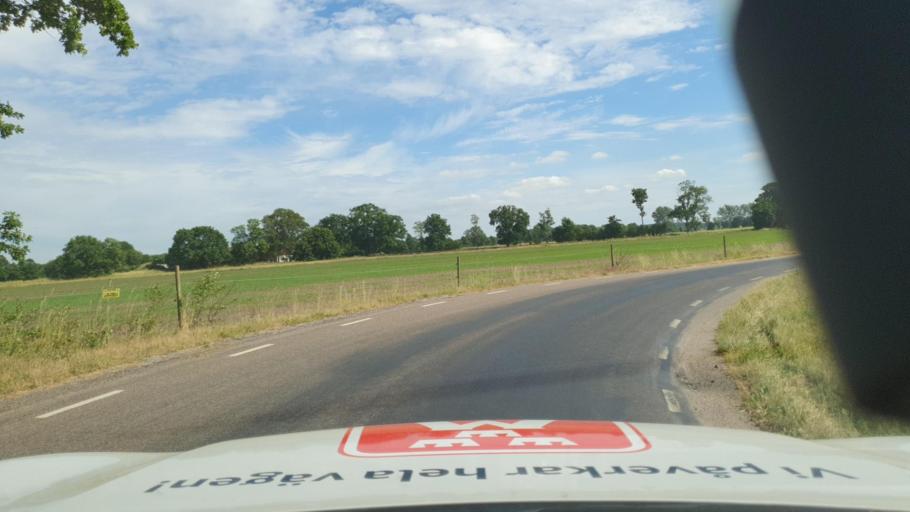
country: SE
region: Skane
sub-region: Sjobo Kommun
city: Blentarp
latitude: 55.6110
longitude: 13.6193
